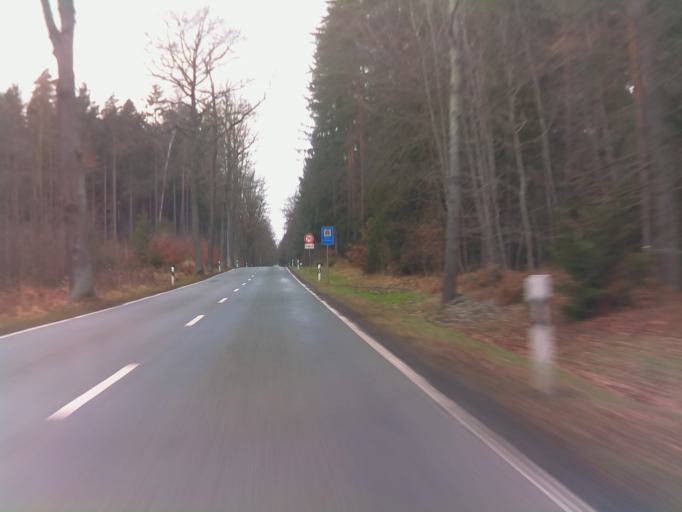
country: DE
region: Thuringia
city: Hummelshain
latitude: 50.7636
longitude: 11.6605
